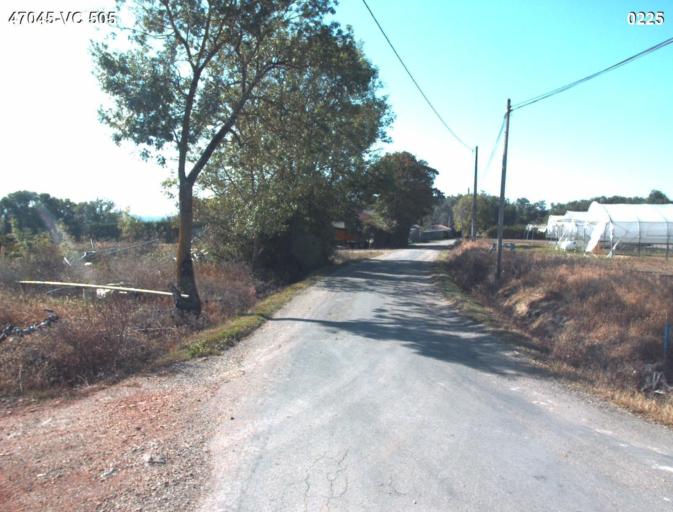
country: FR
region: Aquitaine
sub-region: Departement du Lot-et-Garonne
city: Nerac
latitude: 44.1512
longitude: 0.4000
